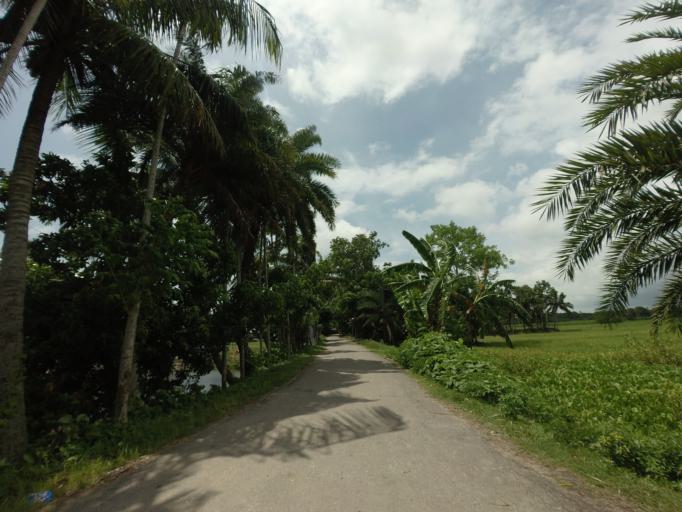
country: BD
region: Khulna
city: Kalia
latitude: 23.0413
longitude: 89.6450
